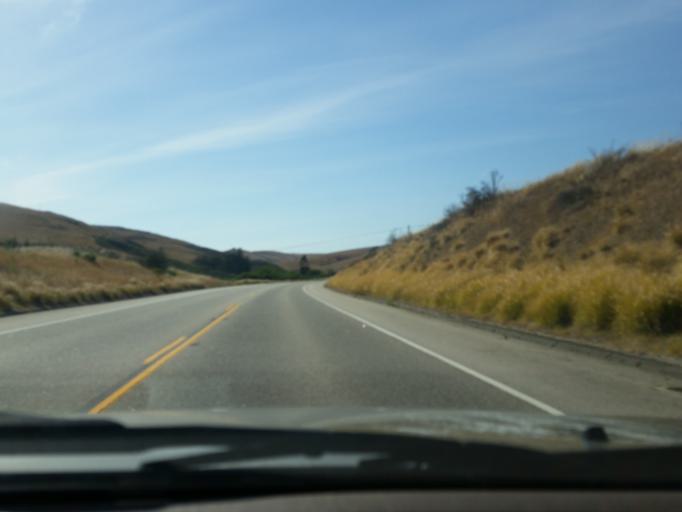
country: US
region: California
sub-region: San Luis Obispo County
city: Cayucos
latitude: 35.4652
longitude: -120.9720
